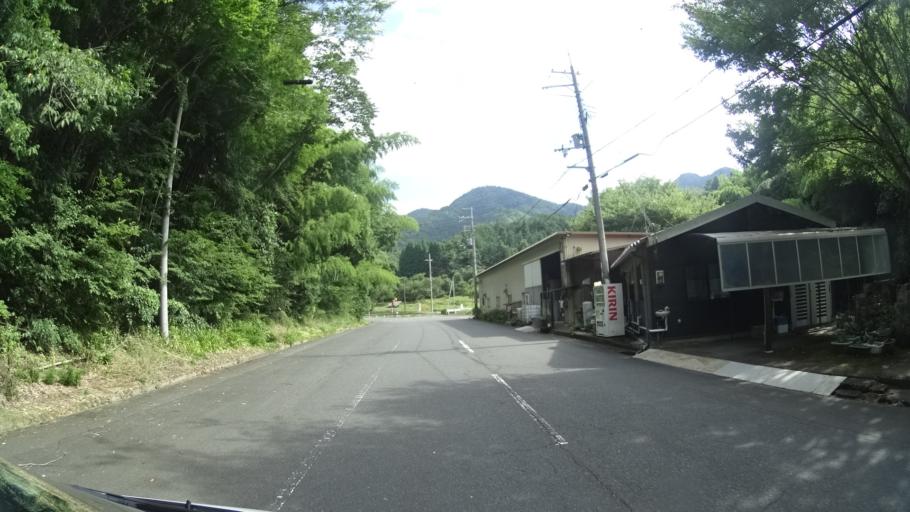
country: JP
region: Kyoto
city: Fukuchiyama
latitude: 35.3626
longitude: 135.1351
